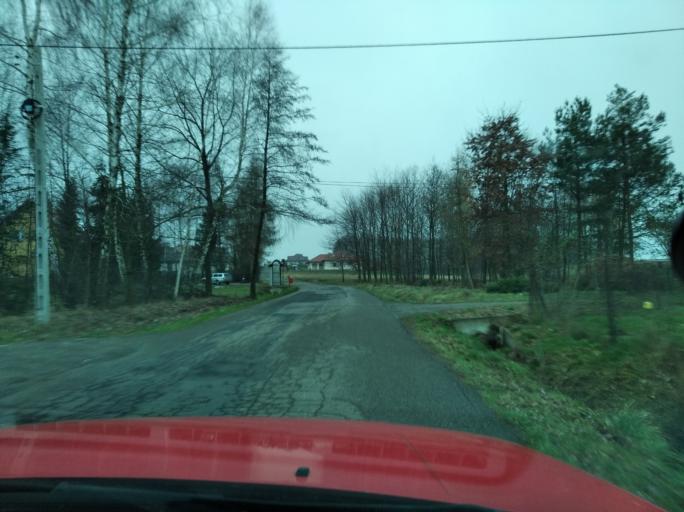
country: PL
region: Subcarpathian Voivodeship
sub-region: Powiat jaroslawski
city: Wierzbna
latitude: 50.0168
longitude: 22.6089
